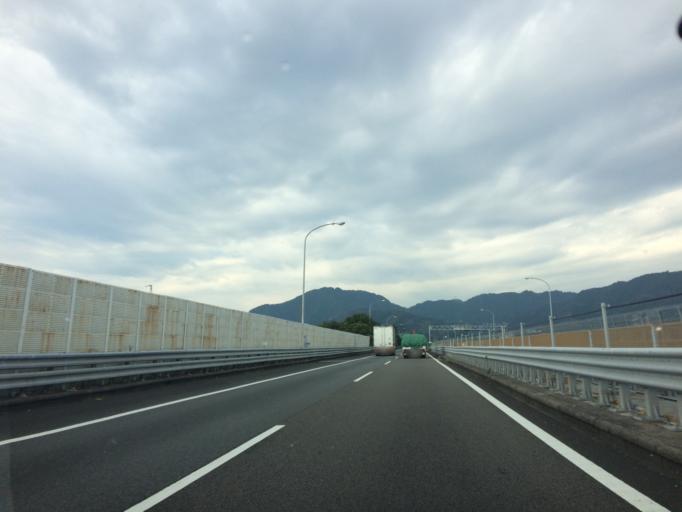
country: JP
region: Shizuoka
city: Shizuoka-shi
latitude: 34.9368
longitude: 138.3769
